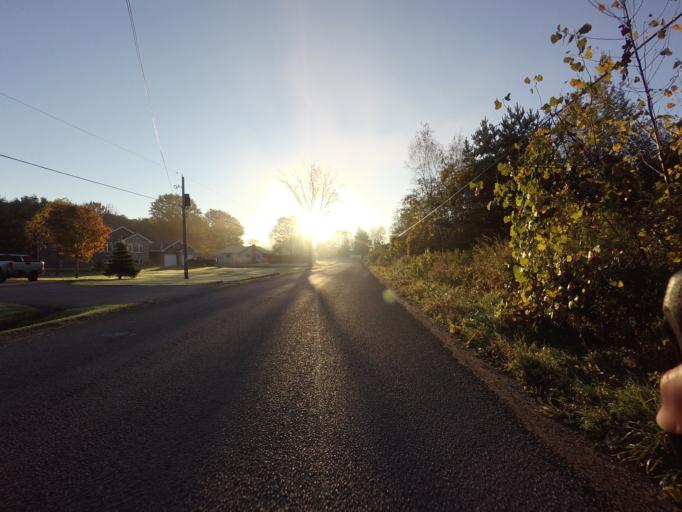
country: CA
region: Ontario
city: Quinte West
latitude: 44.0324
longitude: -77.5741
